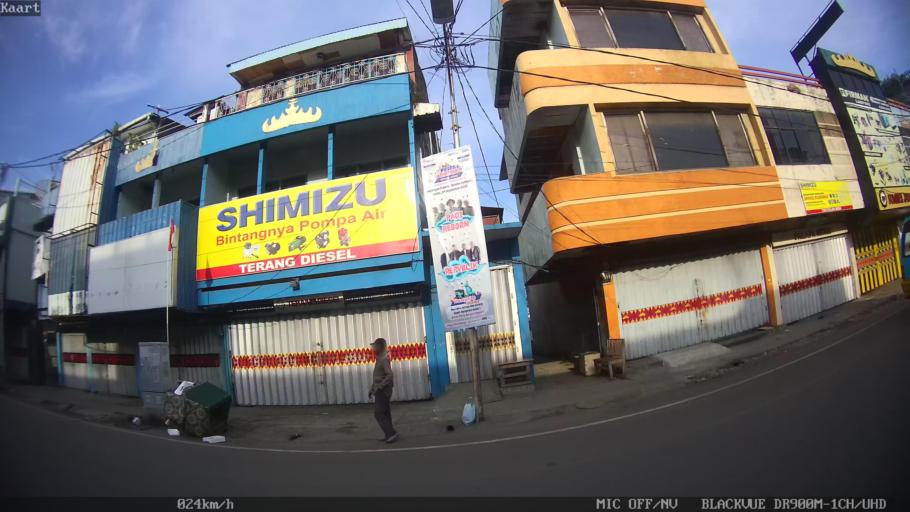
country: ID
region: Lampung
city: Bandarlampung
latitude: -5.4118
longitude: 105.2584
